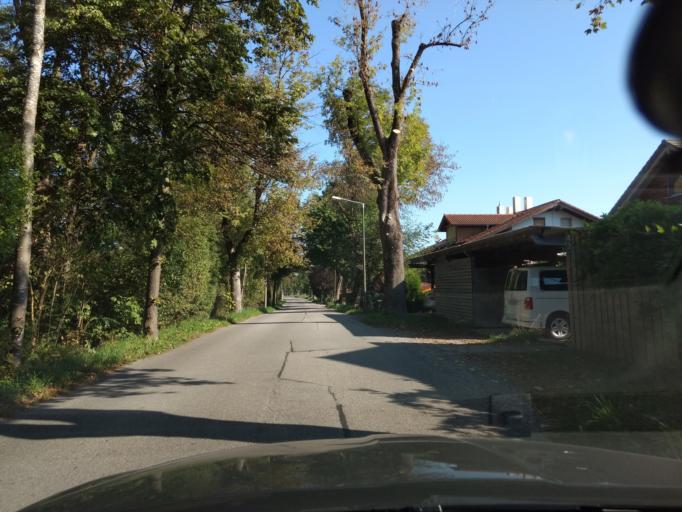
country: DE
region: Bavaria
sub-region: Upper Bavaria
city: Wolfratshausen
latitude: 47.9064
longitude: 11.4220
